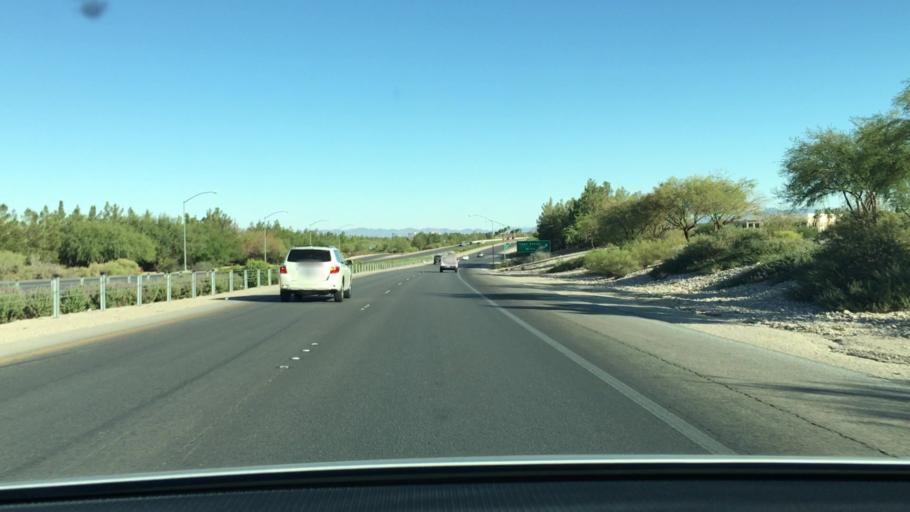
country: US
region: Nevada
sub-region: Clark County
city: Summerlin South
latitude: 36.1909
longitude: -115.3134
